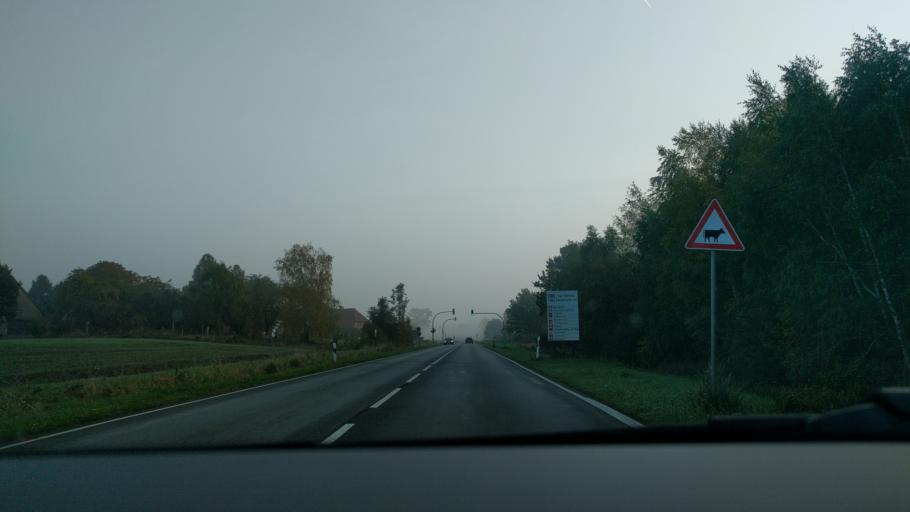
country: DE
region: Lower Saxony
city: Osloss
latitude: 52.4329
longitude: 10.6624
